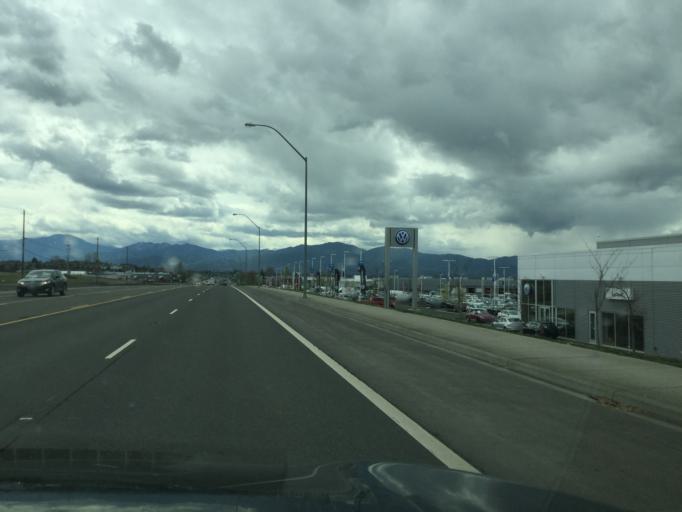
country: US
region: Oregon
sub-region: Jackson County
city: White City
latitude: 42.3822
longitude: -122.8561
